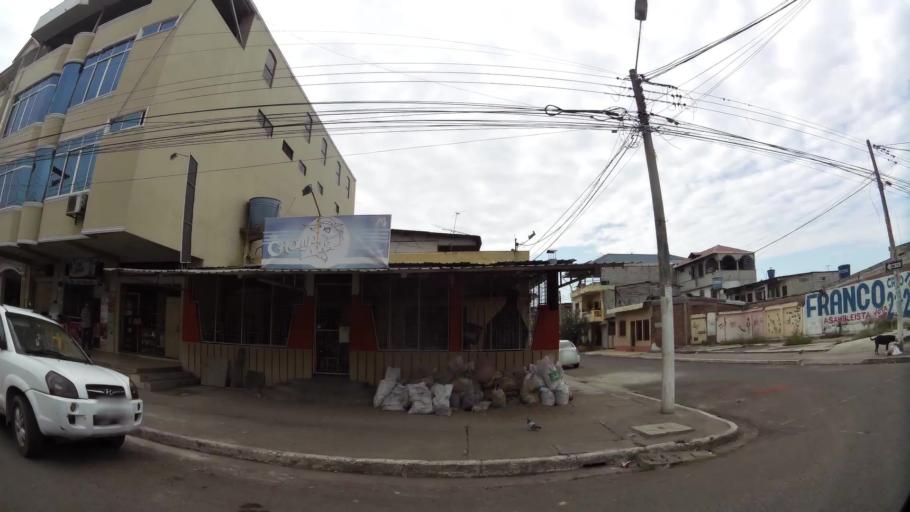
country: EC
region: El Oro
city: Machala
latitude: -3.2541
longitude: -79.9543
